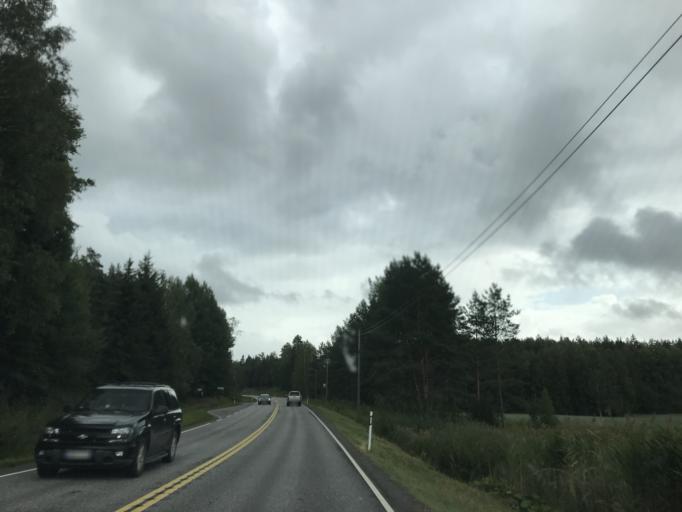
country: FI
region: Varsinais-Suomi
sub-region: Salo
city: Pernioe
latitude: 60.0847
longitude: 23.2319
